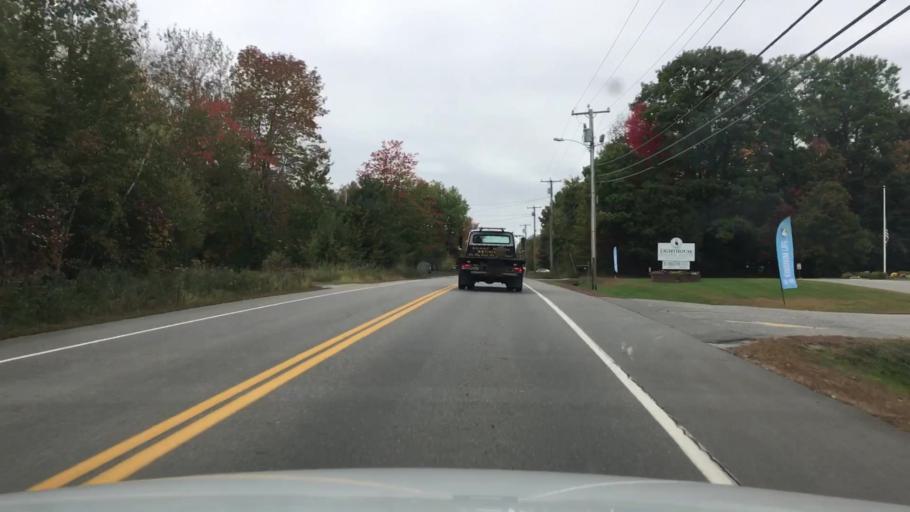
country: US
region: Maine
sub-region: Kennebec County
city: Oakland
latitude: 44.5549
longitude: -69.7361
